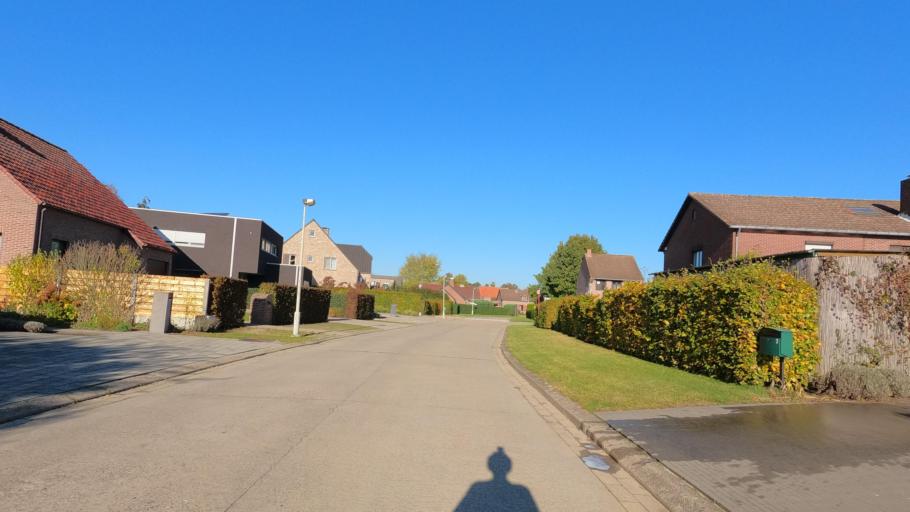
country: BE
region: Flanders
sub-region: Provincie Antwerpen
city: Zoersel
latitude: 51.3006
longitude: 4.6958
